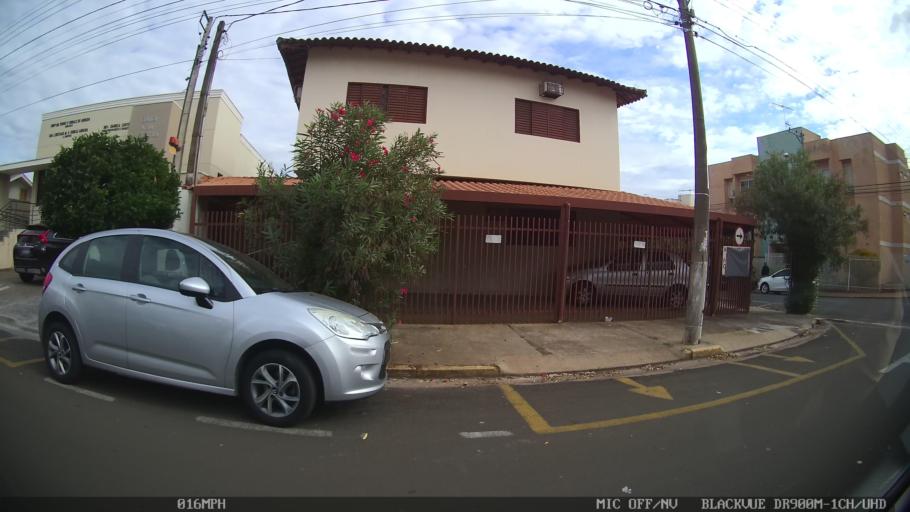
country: BR
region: Sao Paulo
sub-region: Sao Jose Do Rio Preto
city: Sao Jose do Rio Preto
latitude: -20.8306
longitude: -49.4000
